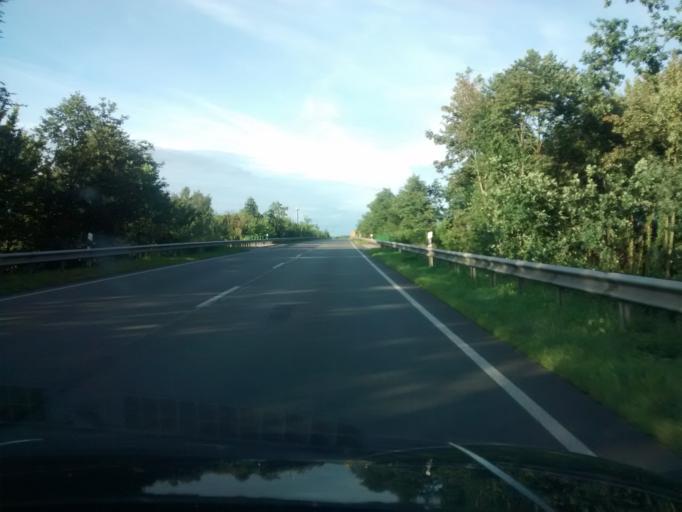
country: DE
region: Lower Saxony
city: Loningen
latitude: 52.7418
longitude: 7.7512
